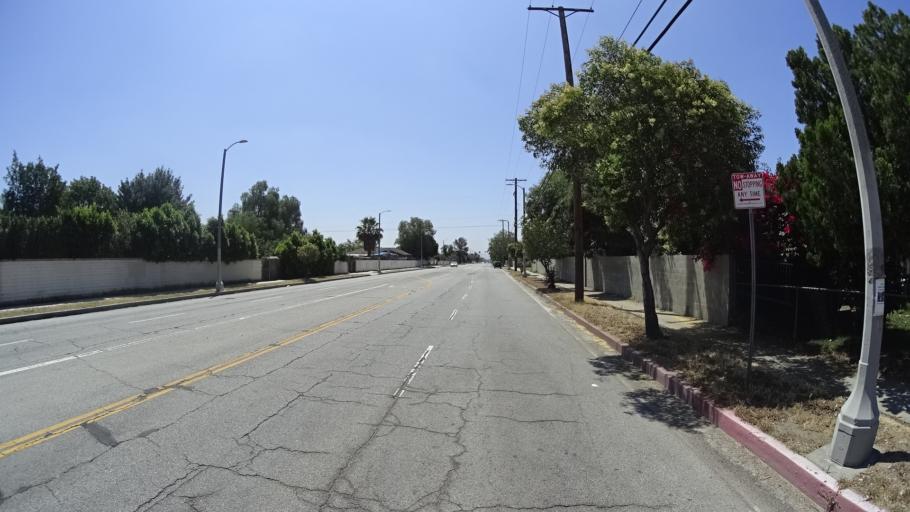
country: US
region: California
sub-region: Los Angeles County
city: San Fernando
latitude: 34.2410
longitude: -118.4251
